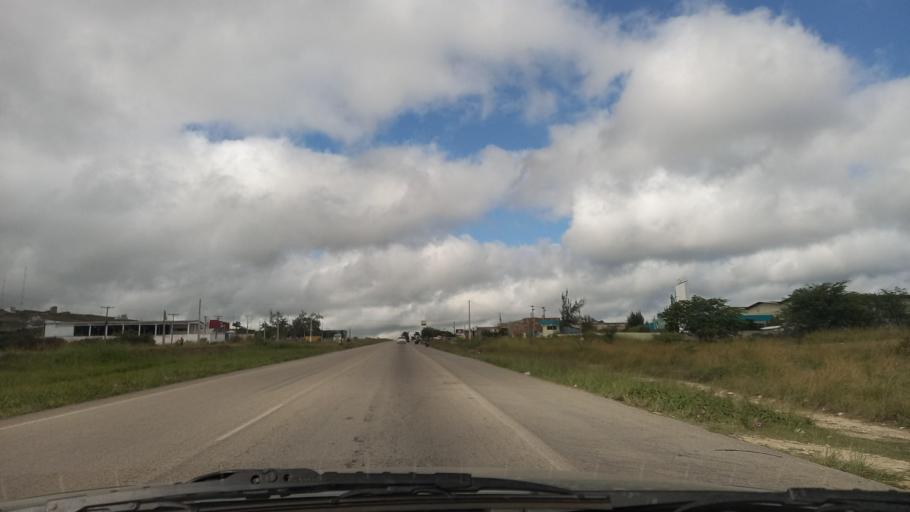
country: BR
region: Pernambuco
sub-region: Caruaru
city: Caruaru
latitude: -8.3063
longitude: -35.9895
